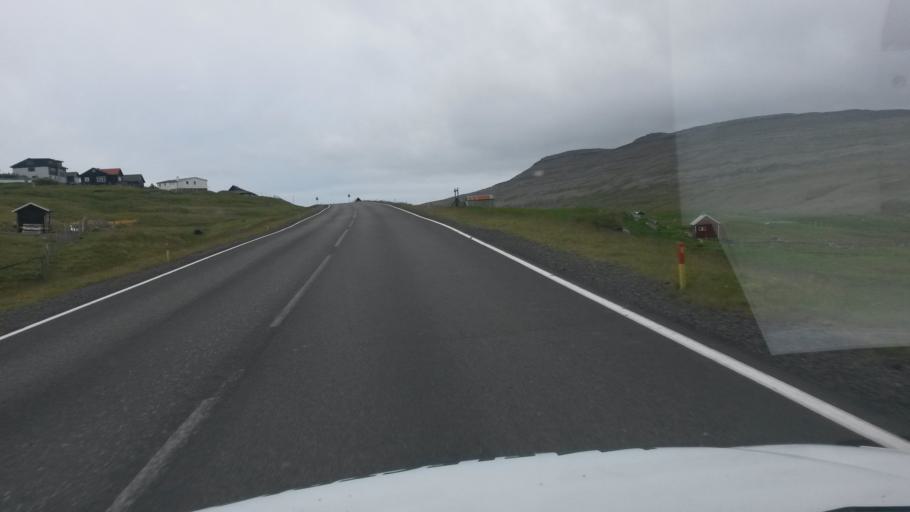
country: FO
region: Streymoy
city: Hoyvik
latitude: 62.0010
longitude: -6.8371
